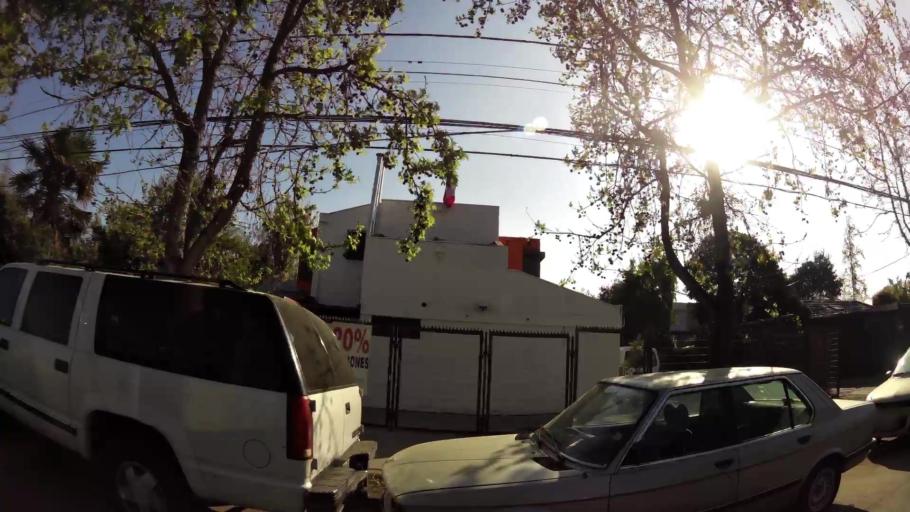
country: CL
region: Santiago Metropolitan
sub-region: Provincia de Santiago
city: Villa Presidente Frei, Nunoa, Santiago, Chile
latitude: -33.3563
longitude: -70.5106
